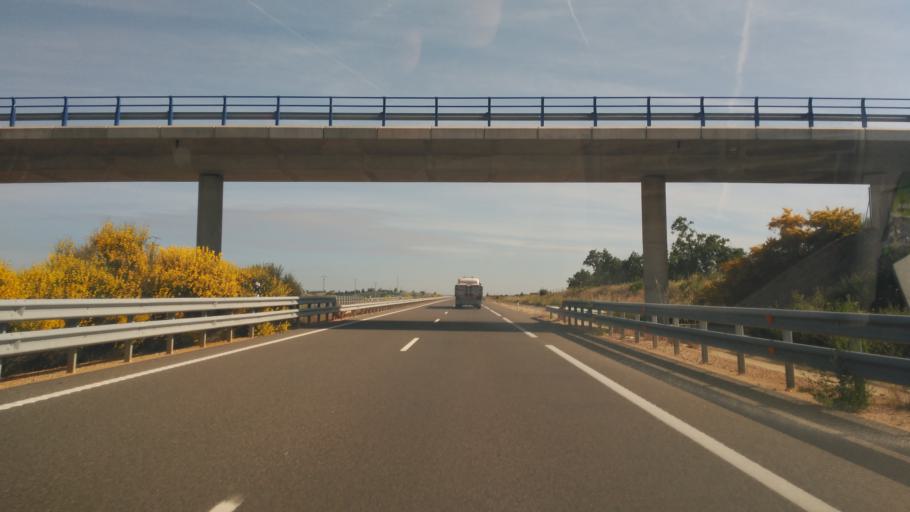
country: ES
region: Castille and Leon
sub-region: Provincia de Salamanca
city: Topas
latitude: 41.1611
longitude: -5.6955
